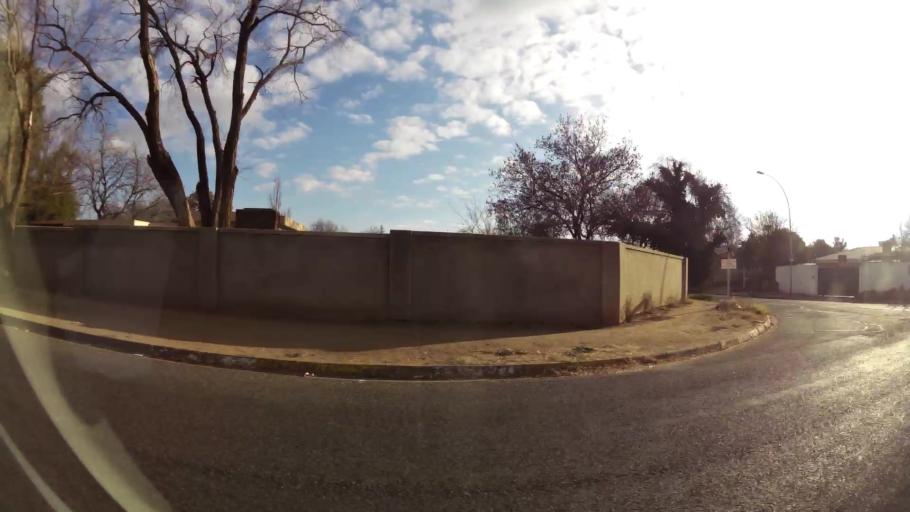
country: ZA
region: Orange Free State
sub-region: Mangaung Metropolitan Municipality
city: Bloemfontein
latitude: -29.1042
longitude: 26.1990
